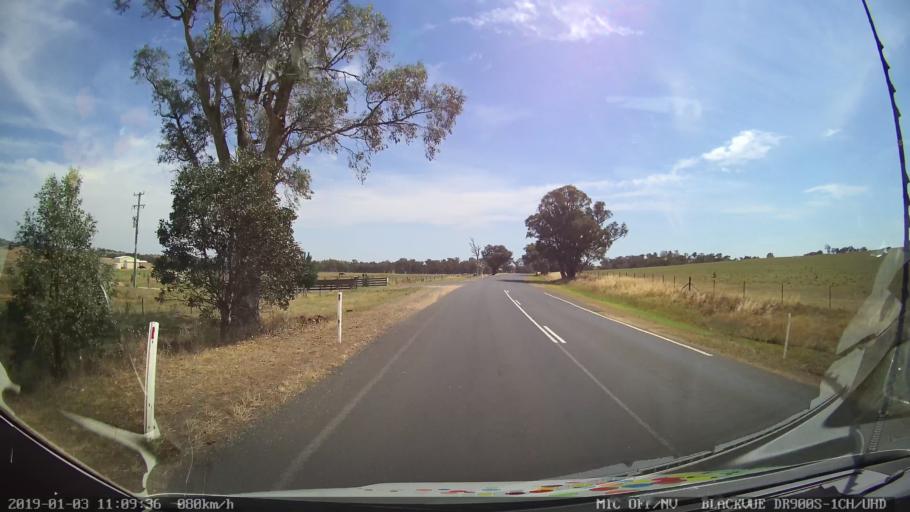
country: AU
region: New South Wales
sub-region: Young
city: Young
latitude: -34.2364
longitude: 148.2555
